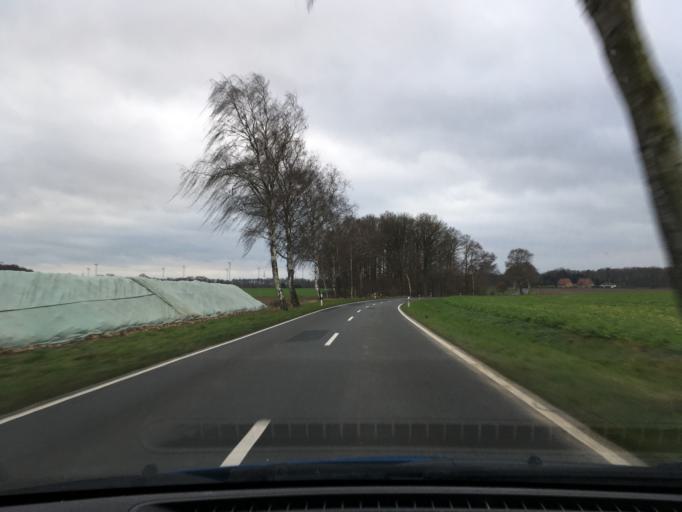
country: DE
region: Lower Saxony
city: Ebstorf
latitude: 53.0094
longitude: 10.4182
